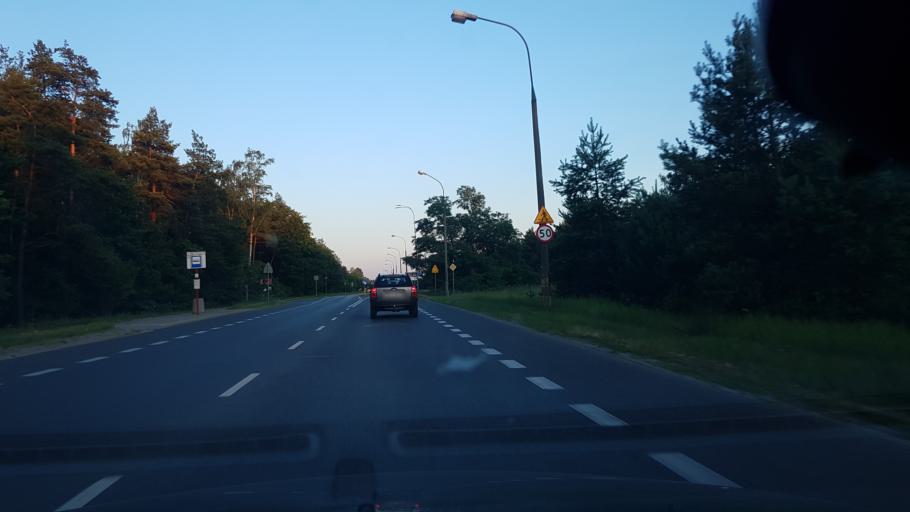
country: PL
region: Masovian Voivodeship
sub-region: Warszawa
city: Wawer
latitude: 52.1990
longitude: 21.1745
